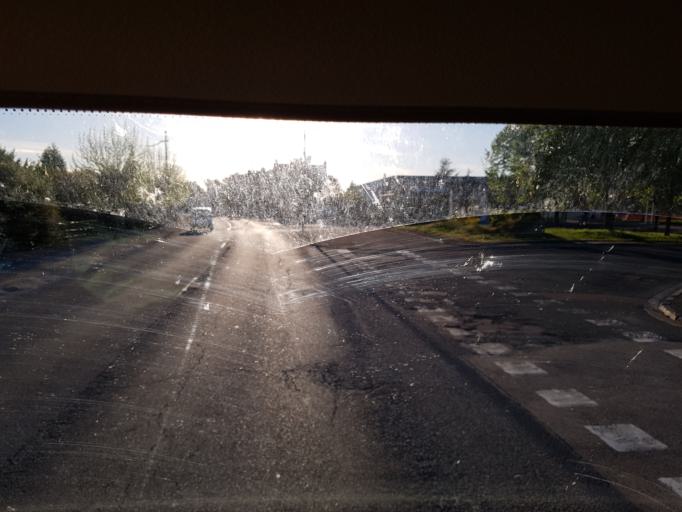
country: FR
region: Champagne-Ardenne
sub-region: Departement de l'Aube
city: Romilly-sur-Seine
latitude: 48.5116
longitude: 3.7208
